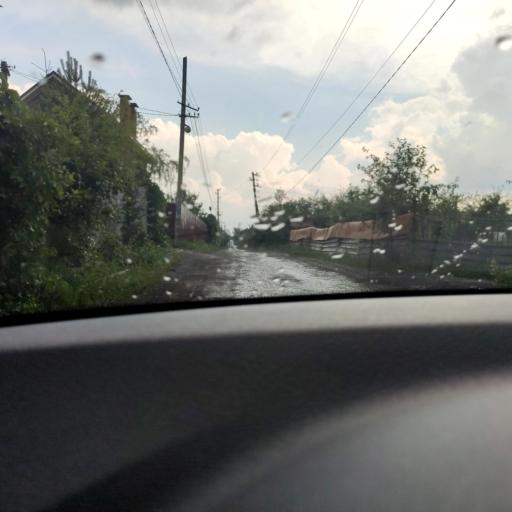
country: RU
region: Samara
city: Novosemeykino
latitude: 53.4022
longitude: 50.3150
